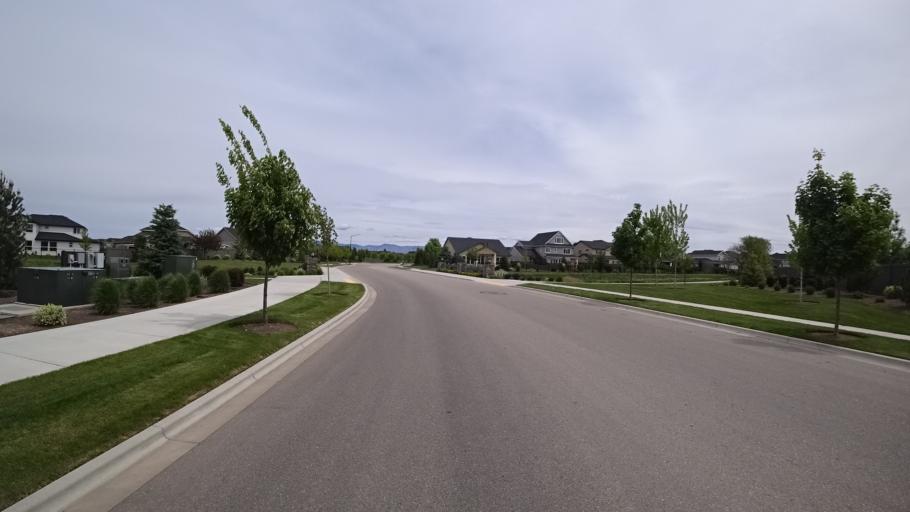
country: US
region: Idaho
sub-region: Ada County
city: Meridian
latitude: 43.5537
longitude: -116.3530
